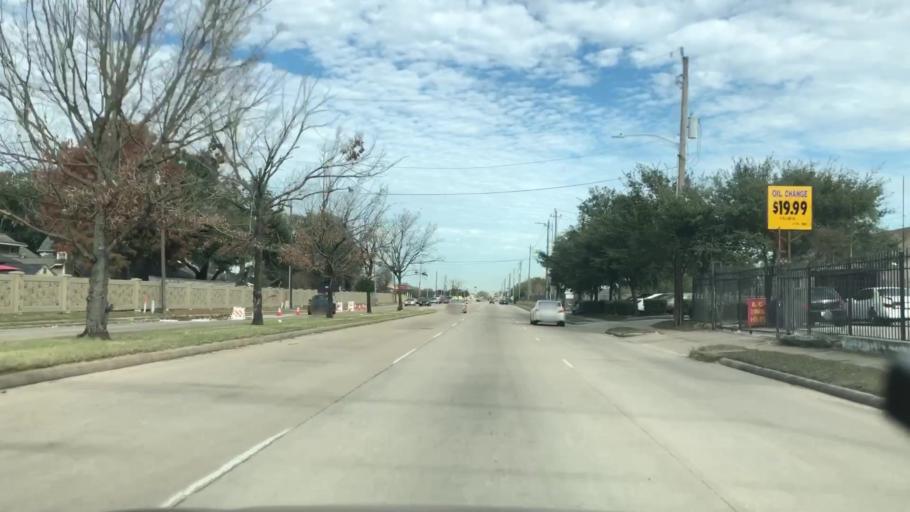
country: US
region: Texas
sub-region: Fort Bend County
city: Missouri City
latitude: 29.6346
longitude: -95.5081
